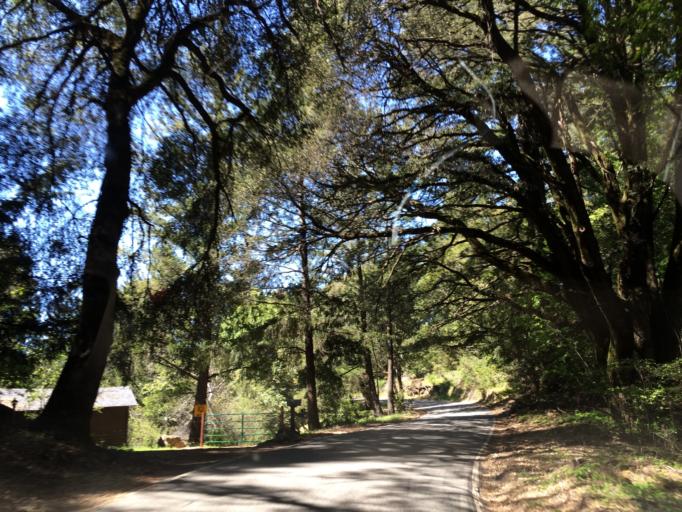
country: US
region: California
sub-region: Santa Clara County
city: Monte Sereno
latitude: 37.1947
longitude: -122.0394
